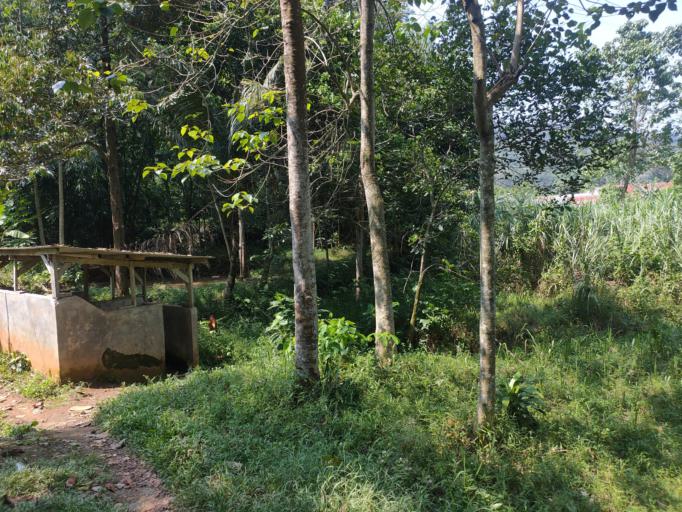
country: ID
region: West Java
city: Ciampea
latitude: -6.5214
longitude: 106.6505
